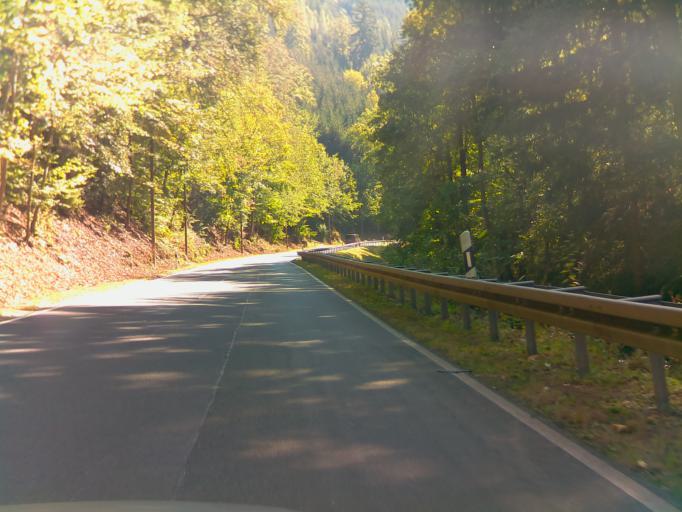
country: DE
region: Thuringia
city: Leutenberg
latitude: 50.5329
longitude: 11.4760
